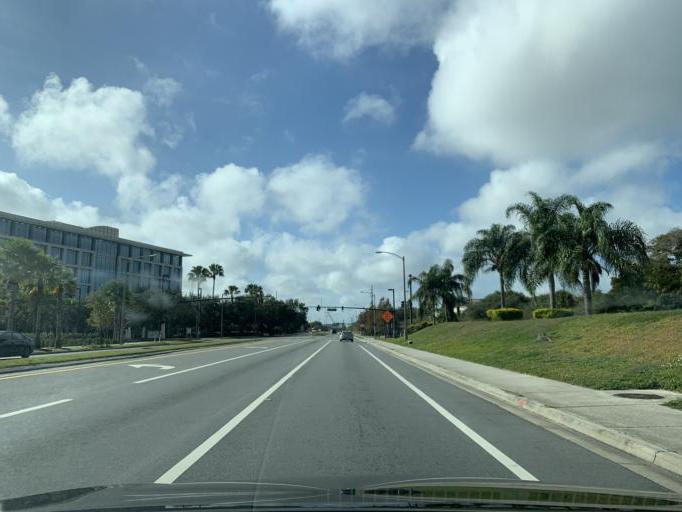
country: US
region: Florida
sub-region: Orange County
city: Oak Ridge
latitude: 28.4892
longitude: -81.4400
